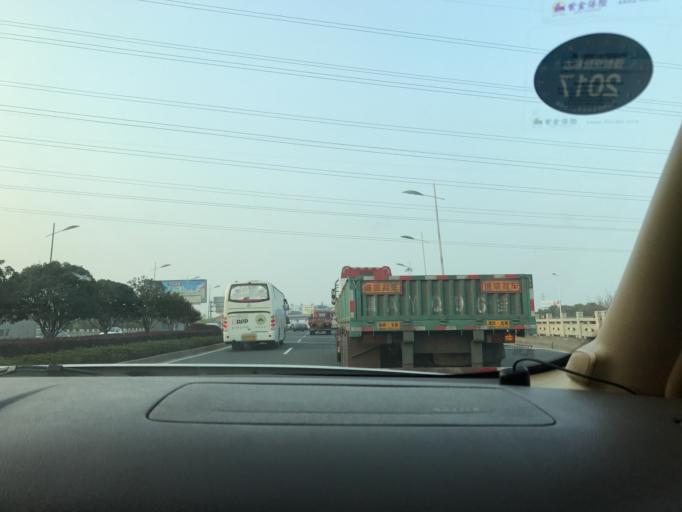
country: CN
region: Jiangsu Sheng
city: Shengpu
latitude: 31.3483
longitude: 120.8308
